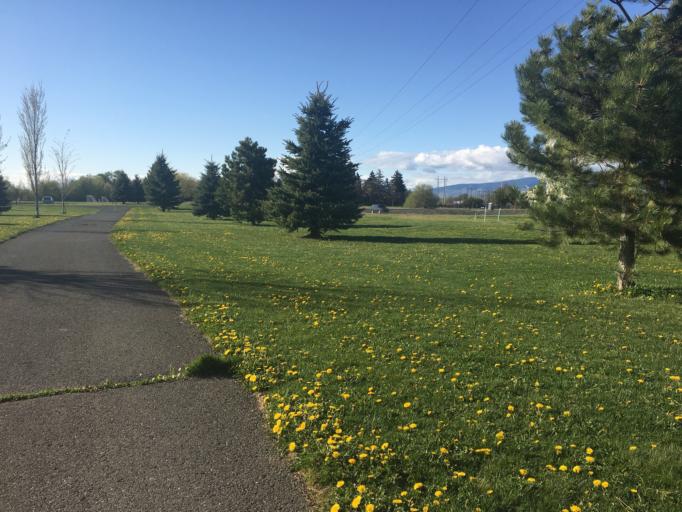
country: US
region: Washington
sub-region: Kittitas County
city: Ellensburg
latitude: 46.9933
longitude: -120.5627
